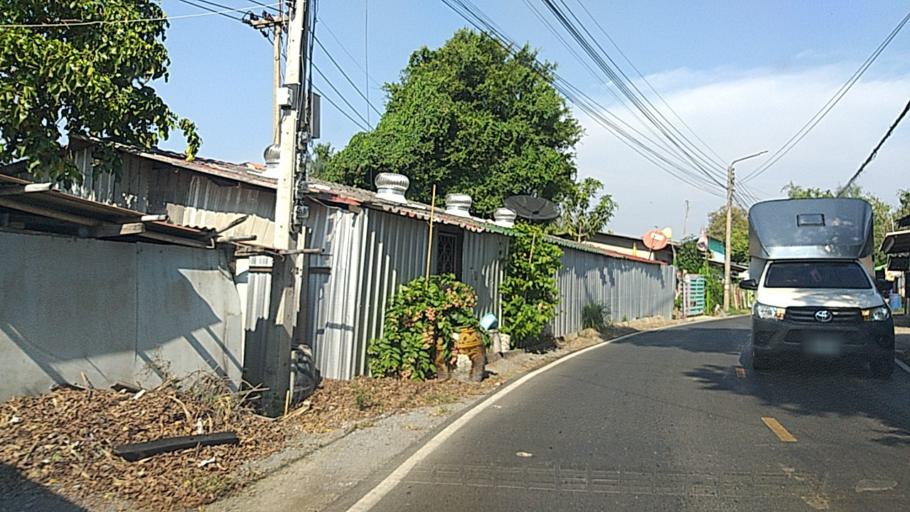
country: TH
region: Nakhon Pathom
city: Salaya
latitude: 13.8056
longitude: 100.3079
